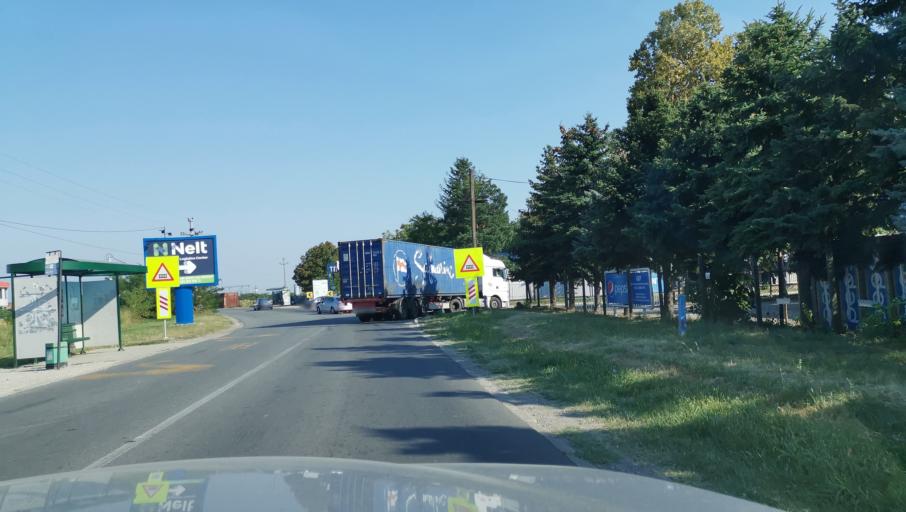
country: RS
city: Dobanovci
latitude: 44.8115
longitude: 20.2424
